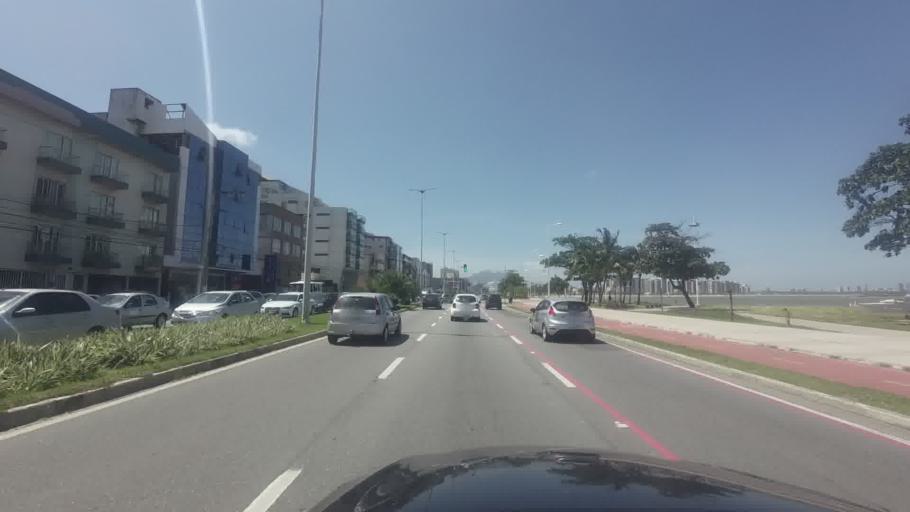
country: BR
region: Espirito Santo
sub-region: Vila Velha
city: Vila Velha
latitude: -20.2912
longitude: -40.2902
